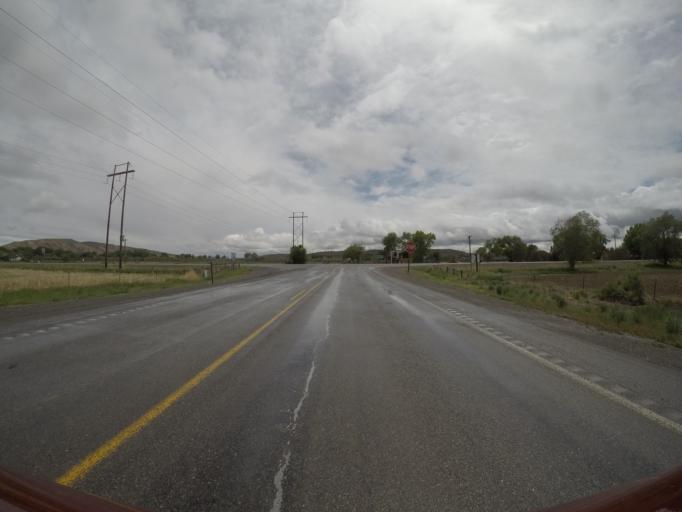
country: US
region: Wyoming
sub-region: Big Horn County
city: Lovell
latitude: 44.8412
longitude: -108.3316
